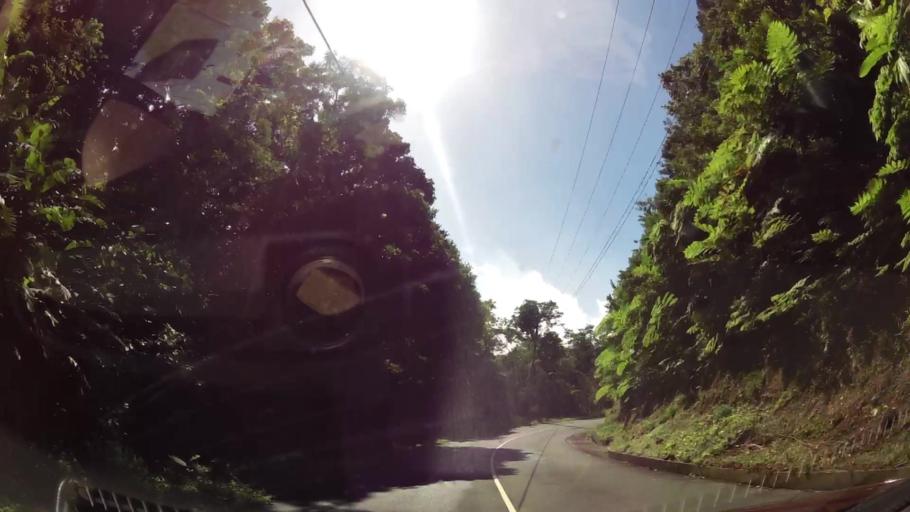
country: DM
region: Saint Paul
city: Pont Casse
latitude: 15.3577
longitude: -61.3560
